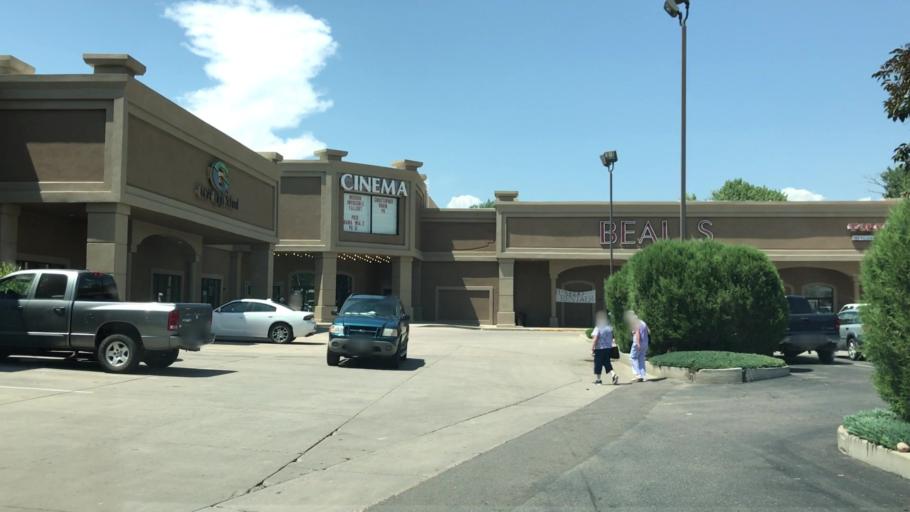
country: US
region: Colorado
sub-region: Fremont County
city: Lincoln Park
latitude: 38.4461
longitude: -105.1843
